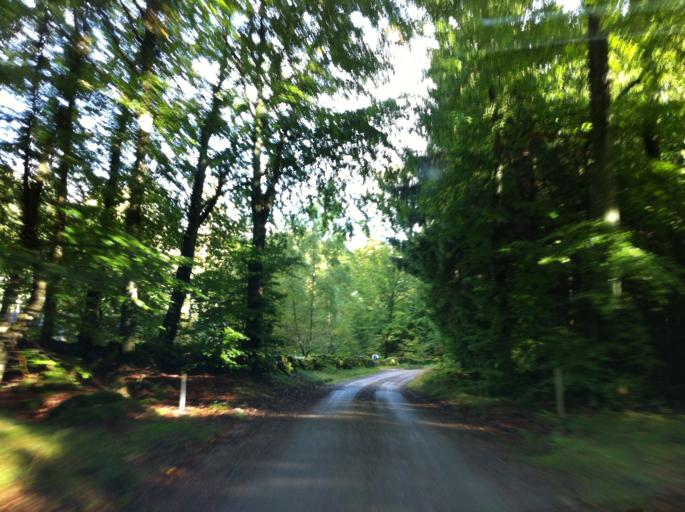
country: SE
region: Skane
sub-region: Hassleholms Kommun
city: Sosdala
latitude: 56.1303
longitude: 13.5829
